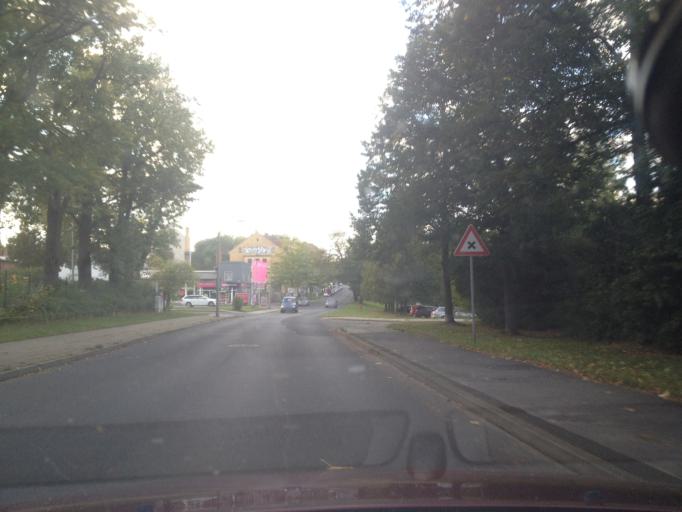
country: DE
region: Saxony
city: Goerlitz
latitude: 51.1595
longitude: 14.9786
